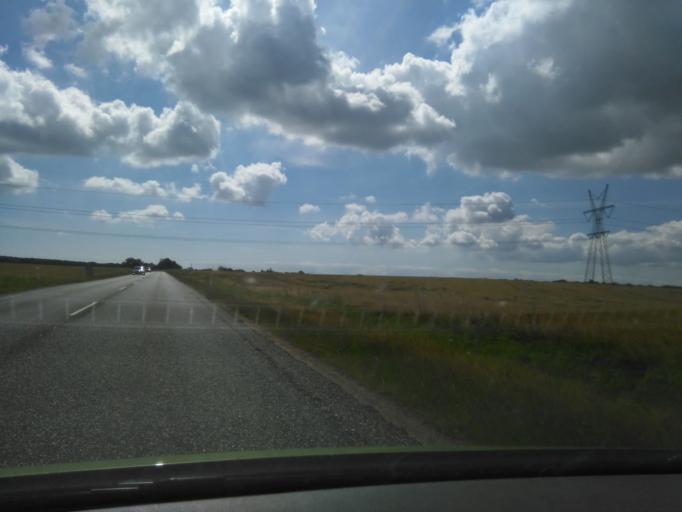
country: DK
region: Central Jutland
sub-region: Arhus Kommune
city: Solbjerg
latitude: 55.9761
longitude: 10.0549
